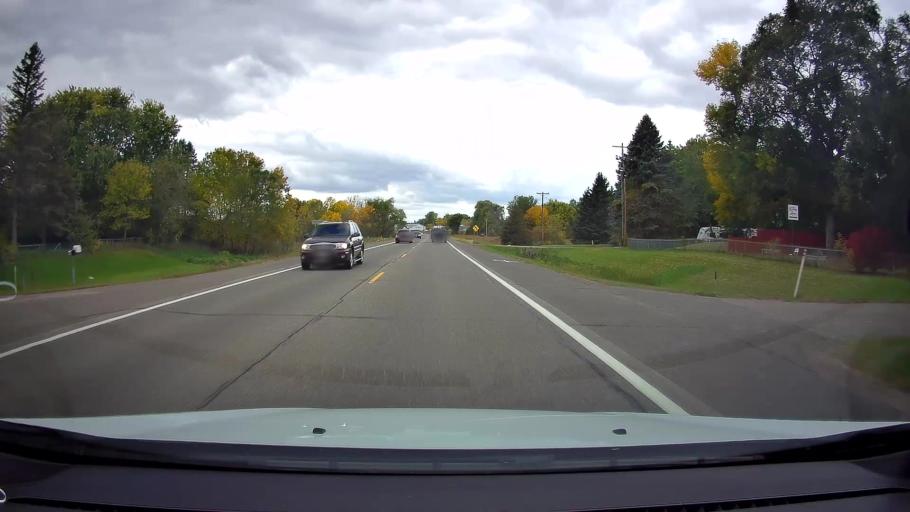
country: US
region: Minnesota
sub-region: Washington County
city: Forest Lake
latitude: 45.3042
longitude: -92.9629
